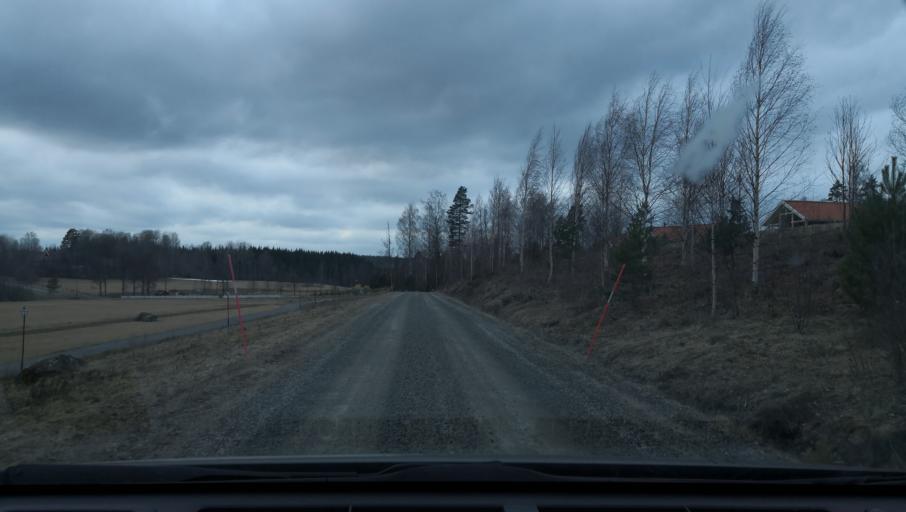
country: SE
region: Vaestmanland
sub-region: Kopings Kommun
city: Kolsva
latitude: 59.6020
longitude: 15.7016
